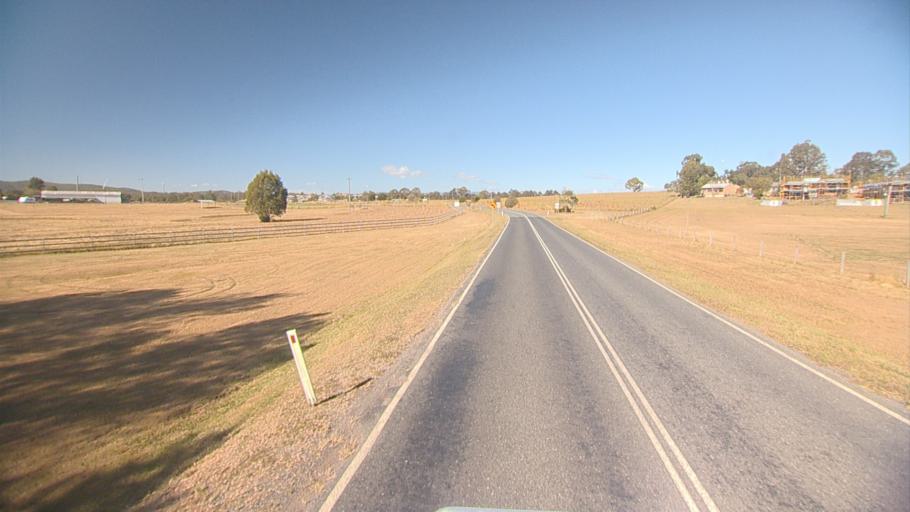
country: AU
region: Queensland
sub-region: Logan
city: Chambers Flat
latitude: -27.7650
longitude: 153.0972
